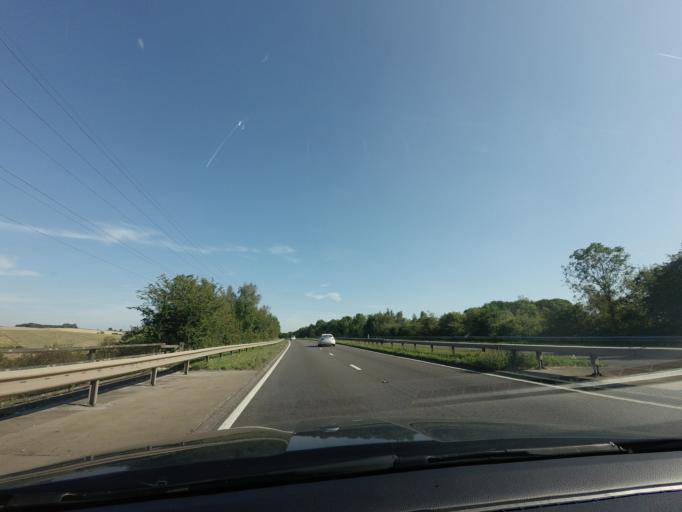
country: GB
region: England
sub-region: Derbyshire
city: Pilsley
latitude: 53.2044
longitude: -1.3701
